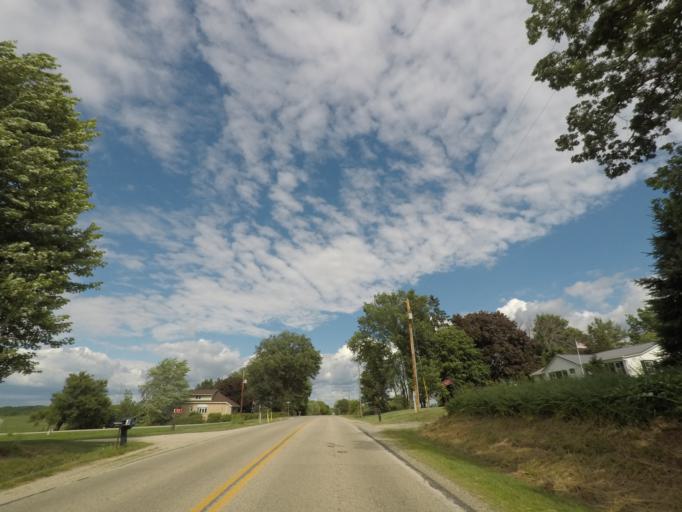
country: US
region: Wisconsin
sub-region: Rock County
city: Janesville
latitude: 42.7012
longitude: -89.0925
